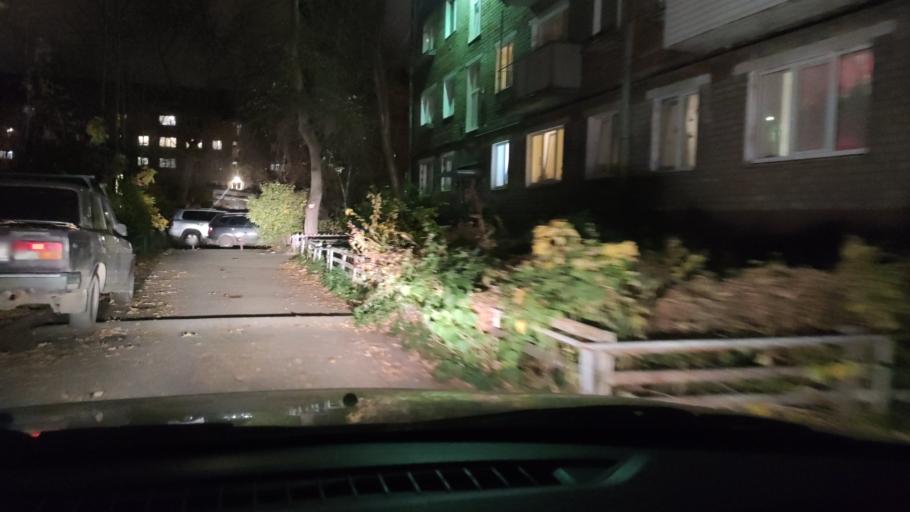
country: RU
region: Perm
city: Perm
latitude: 58.0095
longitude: 56.2025
